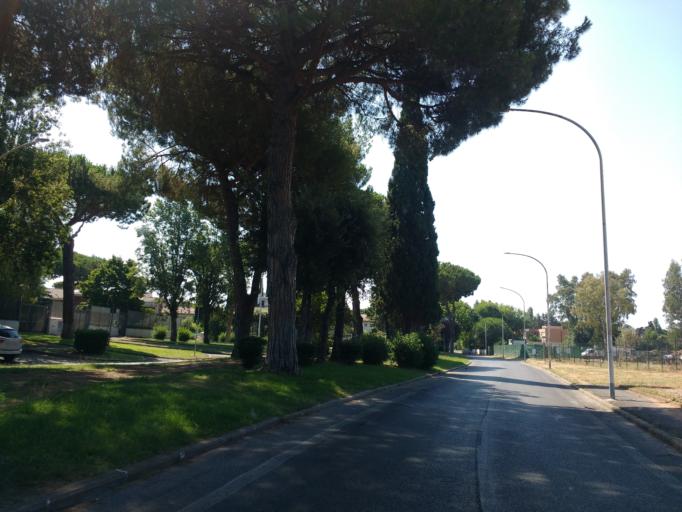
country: IT
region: Latium
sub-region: Citta metropolitana di Roma Capitale
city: Acilia-Castel Fusano-Ostia Antica
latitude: 41.7580
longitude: 12.3600
